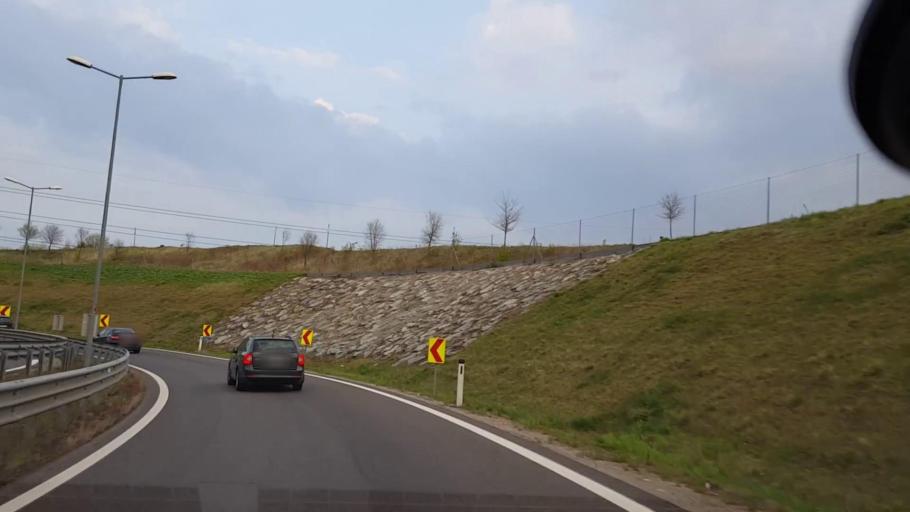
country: AT
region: Lower Austria
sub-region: Politischer Bezirk Wien-Umgebung
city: Leopoldsdorf
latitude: 48.1264
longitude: 16.3856
